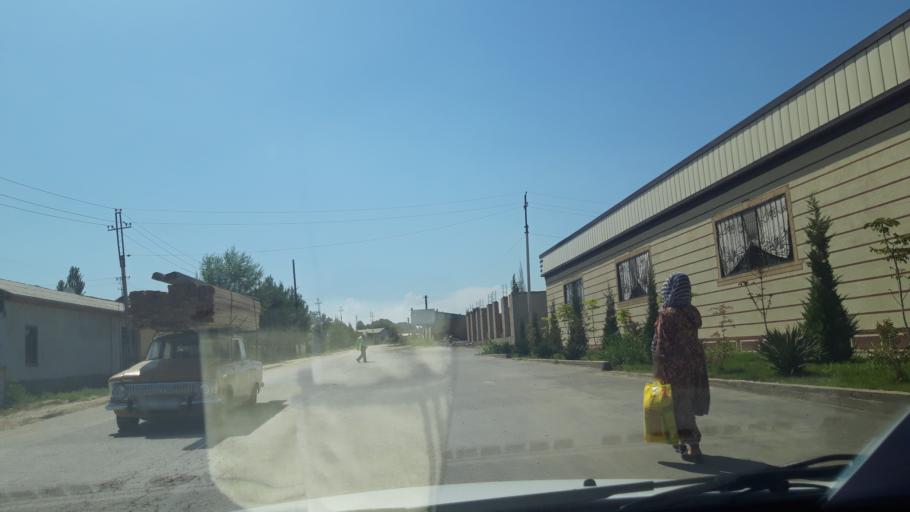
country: UZ
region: Namangan
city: Namangan
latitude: 41.0400
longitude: 71.6958
